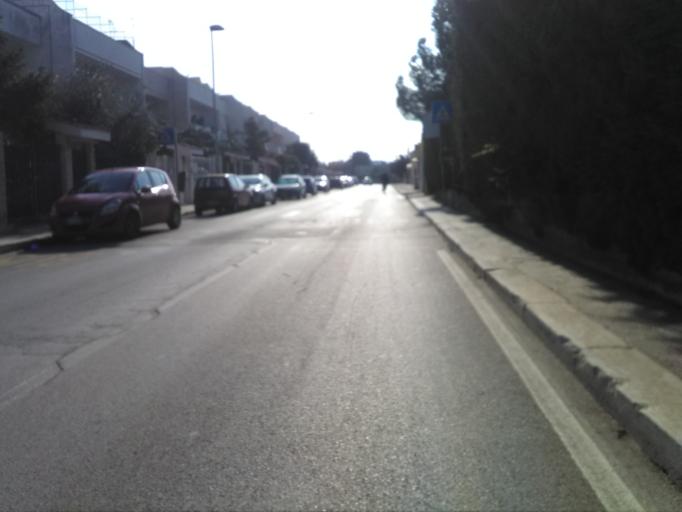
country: IT
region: Apulia
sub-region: Provincia di Bari
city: San Paolo
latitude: 41.1584
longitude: 16.7622
